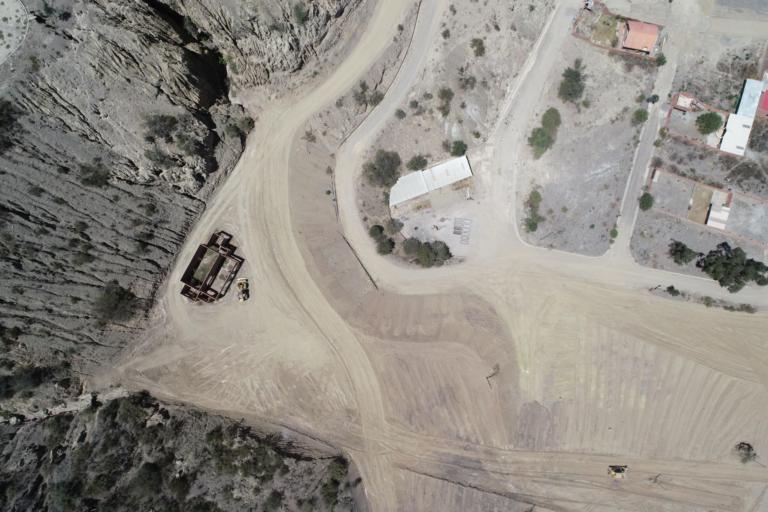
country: BO
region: La Paz
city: La Paz
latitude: -16.6166
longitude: -68.0607
